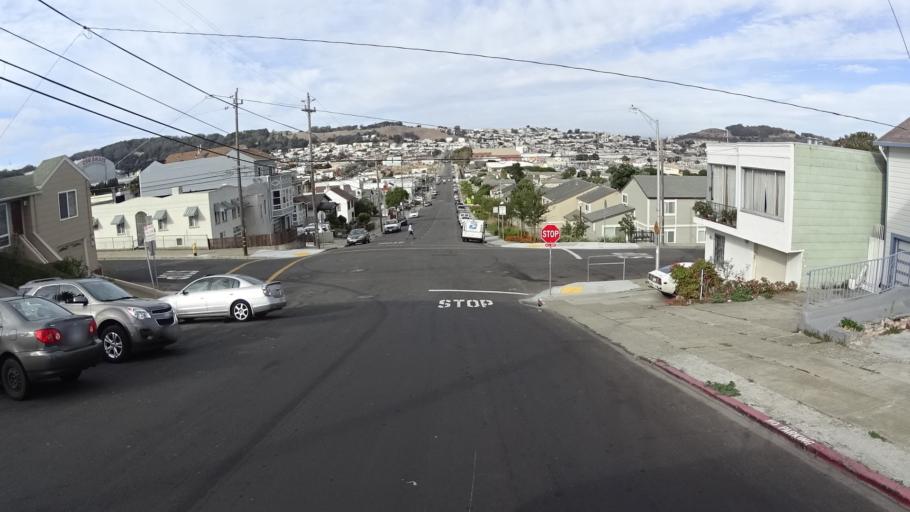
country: US
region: California
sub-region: San Mateo County
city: Brisbane
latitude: 37.7009
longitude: -122.4156
